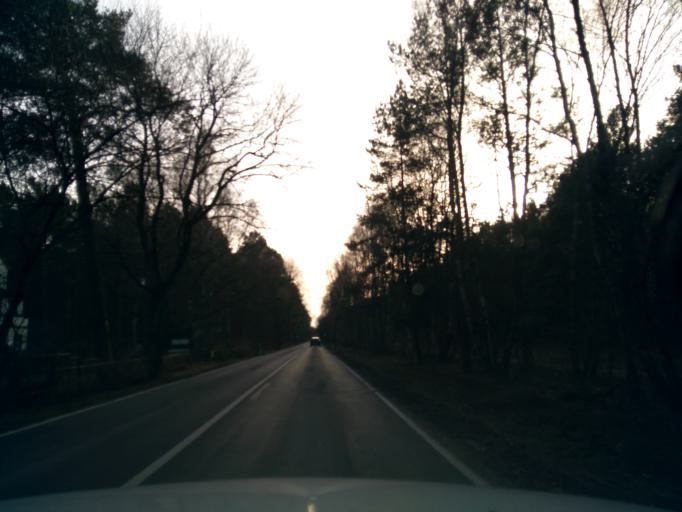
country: DE
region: Brandenburg
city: Birkenwerder
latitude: 52.7199
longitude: 13.3672
